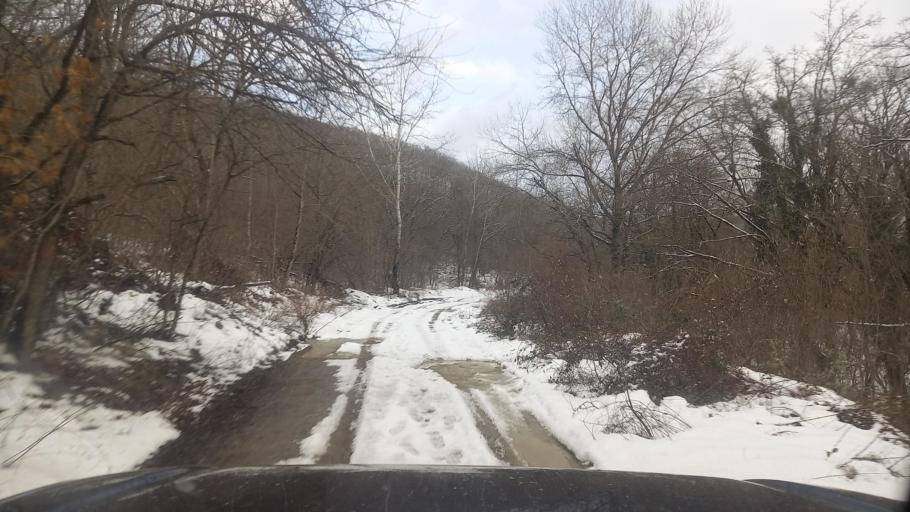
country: RU
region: Krasnodarskiy
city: Smolenskaya
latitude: 44.6894
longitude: 38.8628
